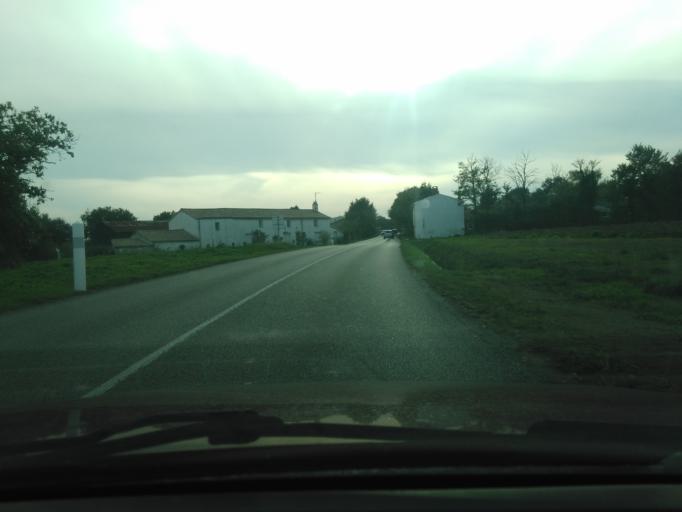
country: FR
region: Pays de la Loire
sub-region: Departement de la Vendee
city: Dompierre-sur-Yon
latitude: 46.7183
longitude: -1.4059
